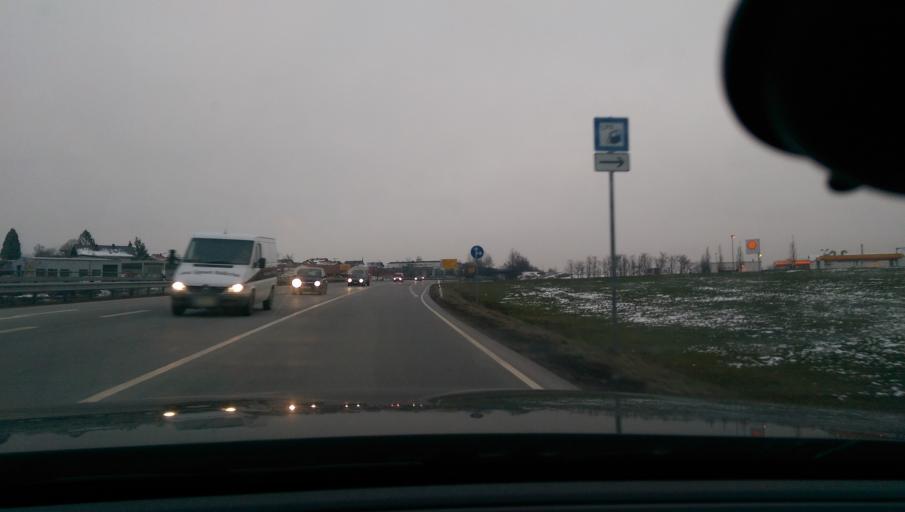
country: DE
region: Bavaria
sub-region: Lower Bavaria
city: Salzweg
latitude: 48.6218
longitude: 13.4790
